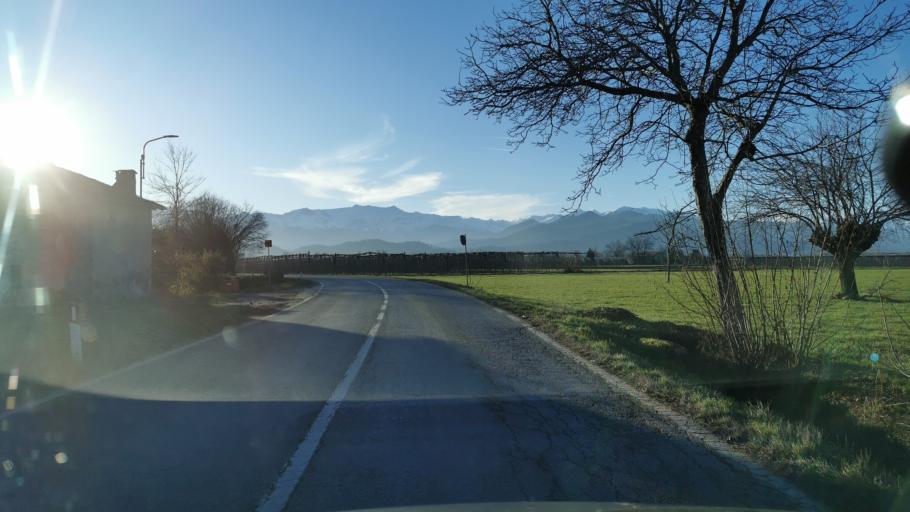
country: IT
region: Piedmont
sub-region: Provincia di Cuneo
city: Caraglio
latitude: 44.4380
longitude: 7.4609
